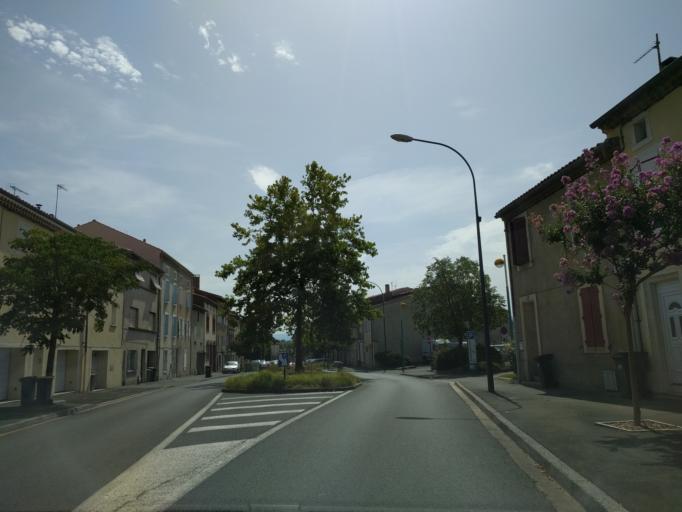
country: FR
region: Midi-Pyrenees
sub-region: Departement du Tarn
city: Castres
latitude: 43.6113
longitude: 2.2360
